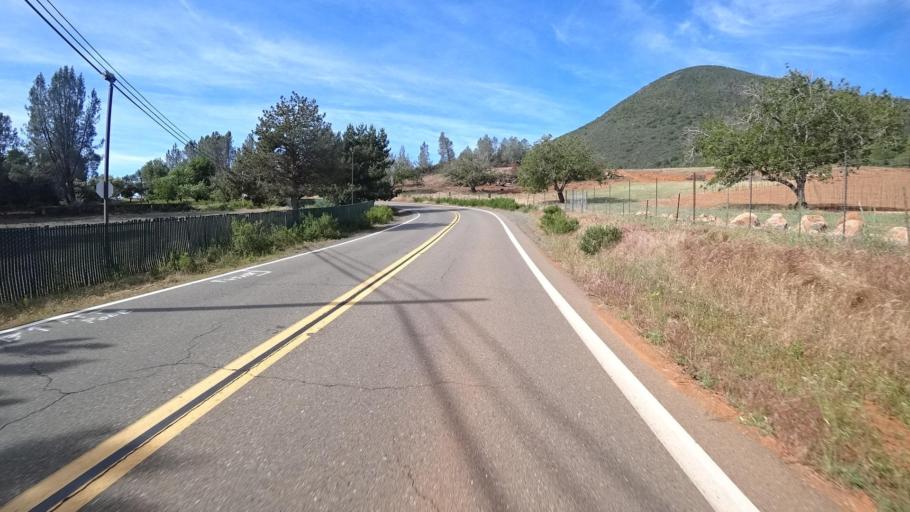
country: US
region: California
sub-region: Lake County
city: Soda Bay
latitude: 38.9845
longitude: -122.7417
